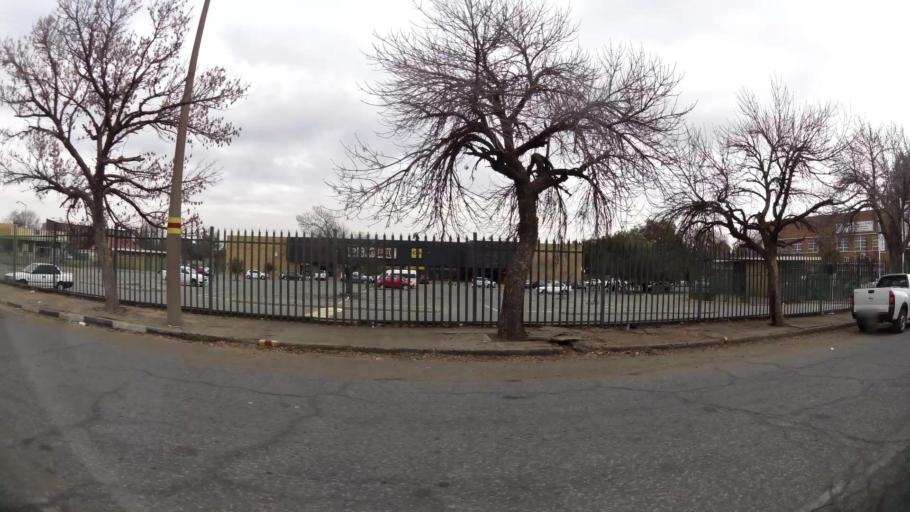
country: ZA
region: Orange Free State
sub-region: Fezile Dabi District Municipality
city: Kroonstad
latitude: -27.6655
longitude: 27.2332
